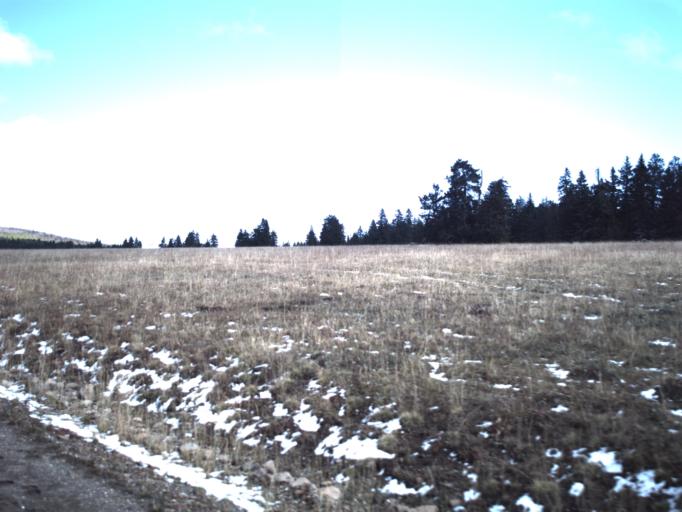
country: US
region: Utah
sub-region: Piute County
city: Junction
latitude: 38.2732
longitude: -112.3661
